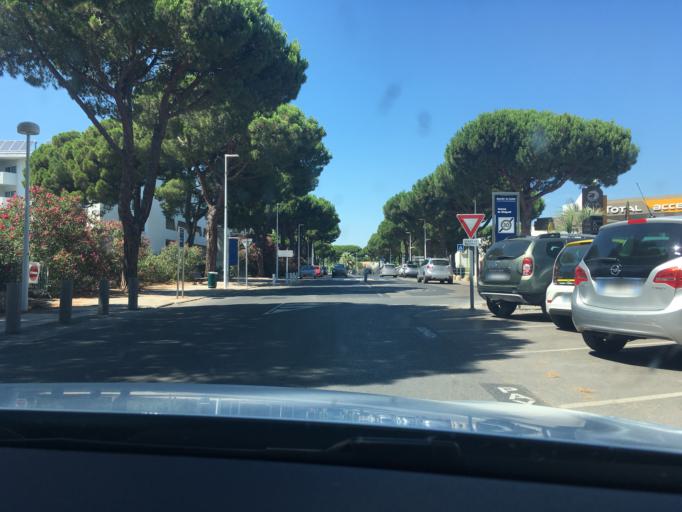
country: FR
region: Languedoc-Roussillon
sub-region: Departement de l'Herault
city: La Grande-Motte
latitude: 43.5615
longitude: 4.0875
